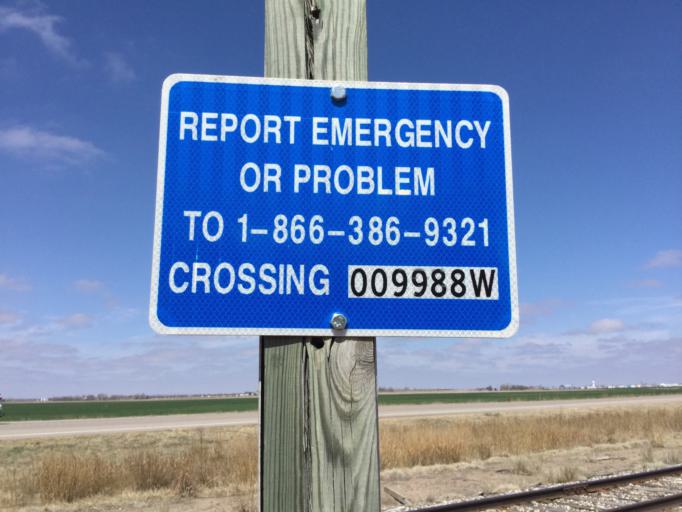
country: US
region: Kansas
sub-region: Barton County
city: Great Bend
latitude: 38.3180
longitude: -98.8695
